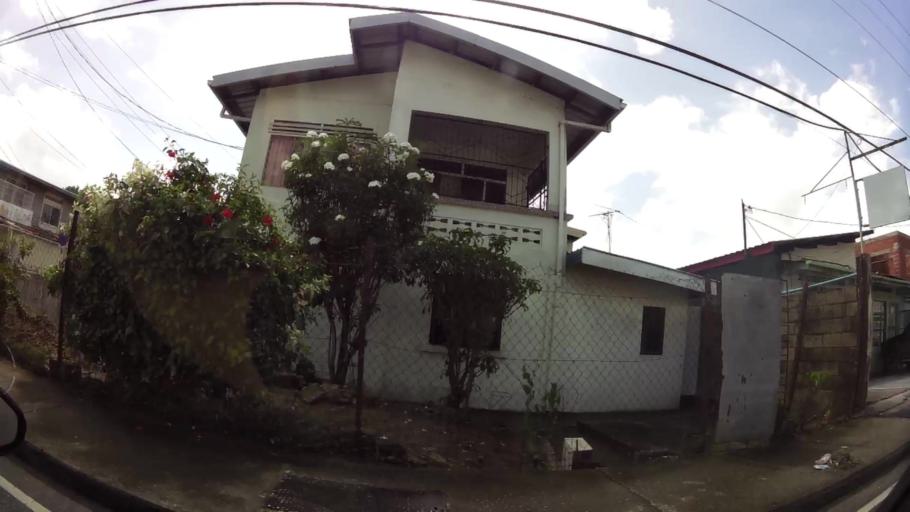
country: TT
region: Borough of Arima
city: Arima
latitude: 10.6385
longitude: -61.2778
